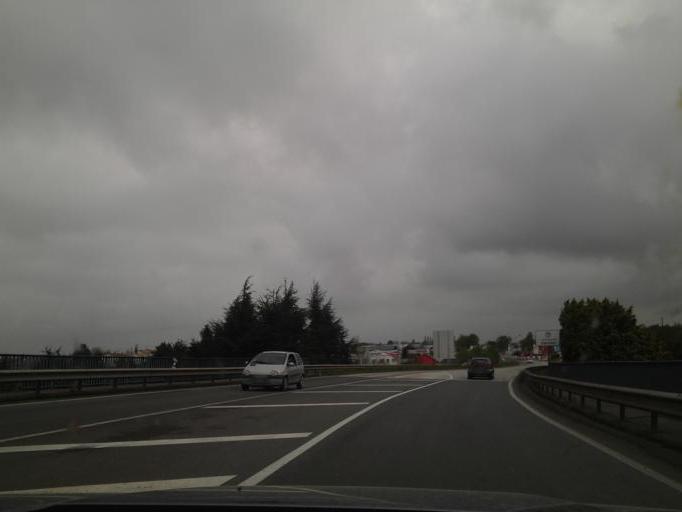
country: FR
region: Pays de la Loire
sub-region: Departement de la Vendee
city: Fontenay-le-Comte
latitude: 46.4481
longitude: -0.8124
